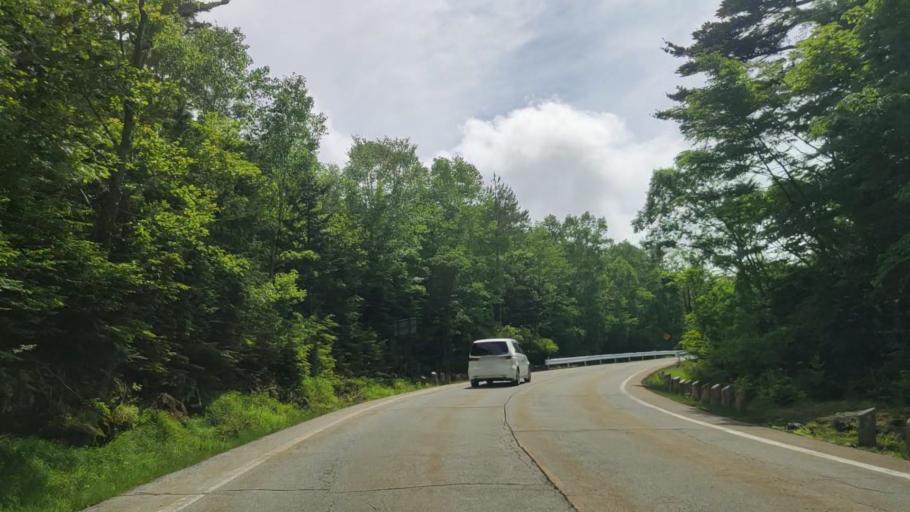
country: JP
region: Yamanashi
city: Fujikawaguchiko
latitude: 35.4071
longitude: 138.6957
